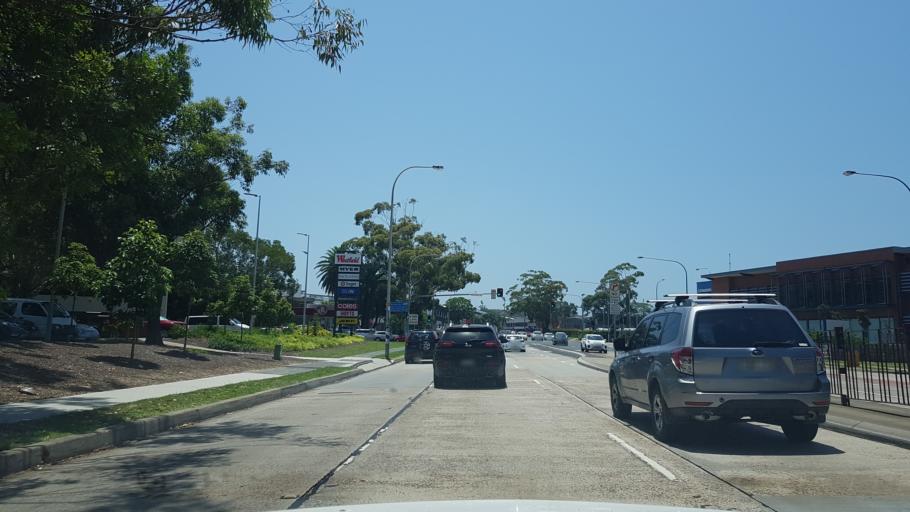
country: AU
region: New South Wales
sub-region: Warringah
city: Brookvale
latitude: -33.7669
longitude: 151.2689
